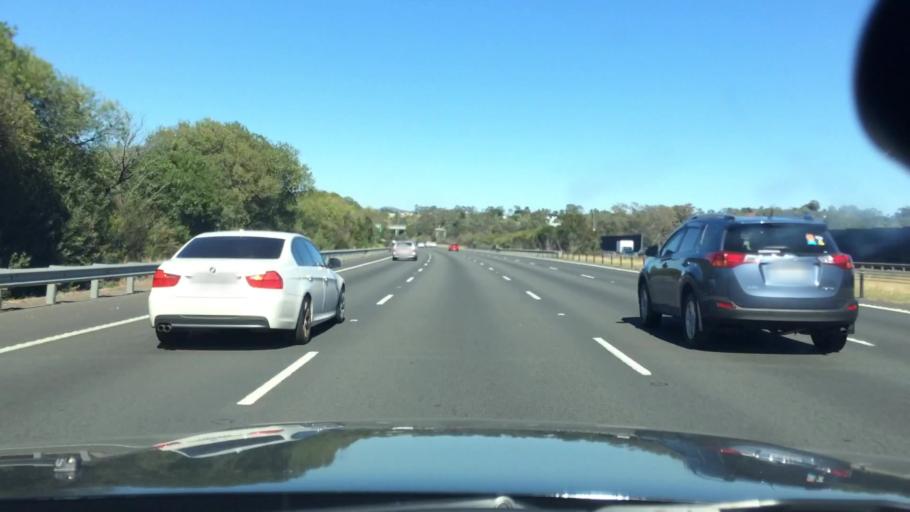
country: AU
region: New South Wales
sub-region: Campbelltown Municipality
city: Denham Court
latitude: -33.9849
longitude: 150.8584
